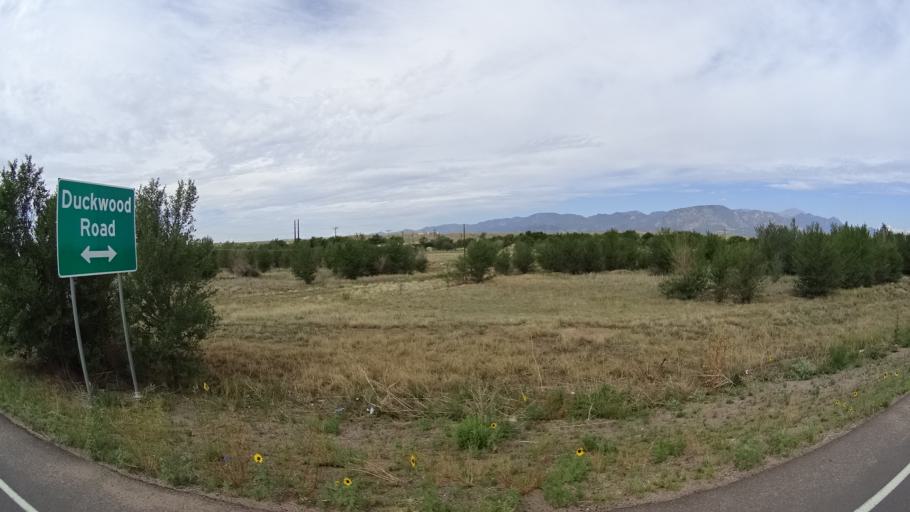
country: US
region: Colorado
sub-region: El Paso County
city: Fountain
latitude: 38.7118
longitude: -104.7127
